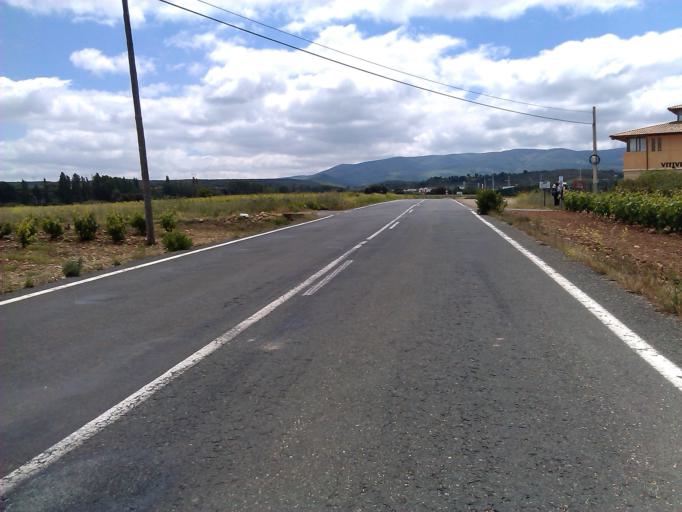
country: ES
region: La Rioja
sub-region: Provincia de La Rioja
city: Hornos de Moncalvillo
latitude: 42.4152
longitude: -2.5925
